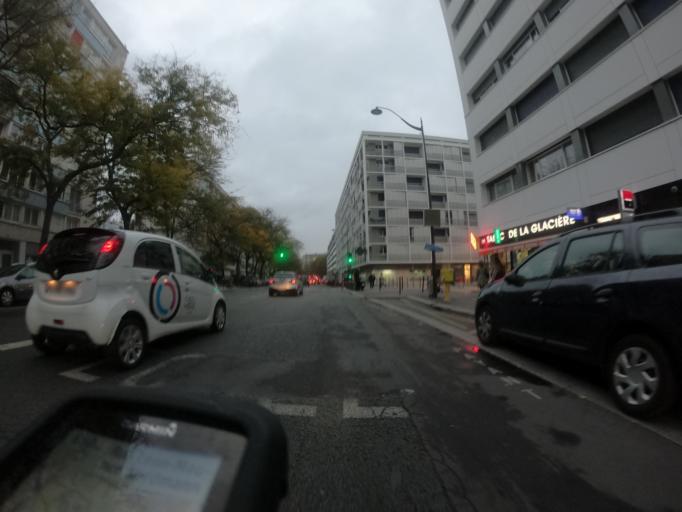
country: FR
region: Ile-de-France
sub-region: Departement du Val-de-Marne
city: Gentilly
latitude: 48.8289
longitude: 2.3431
